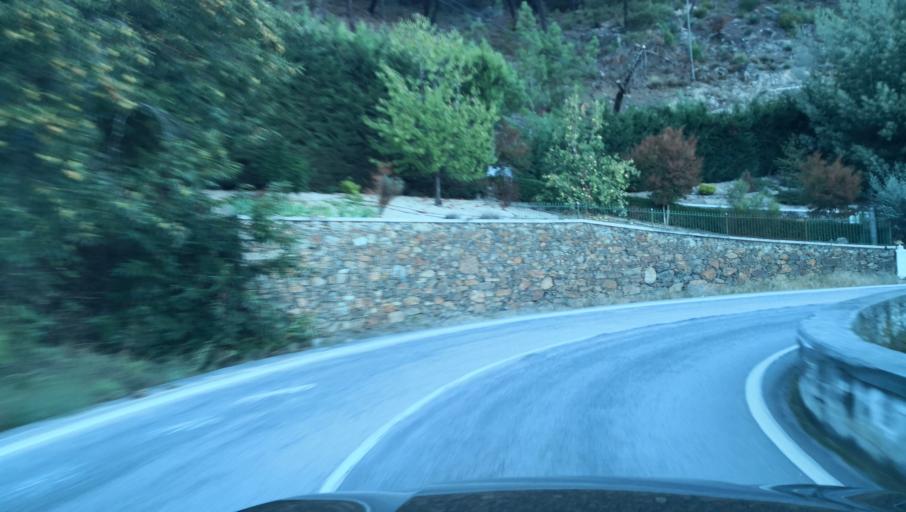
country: PT
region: Vila Real
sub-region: Vila Real
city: Vila Real
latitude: 41.2594
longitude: -7.7740
